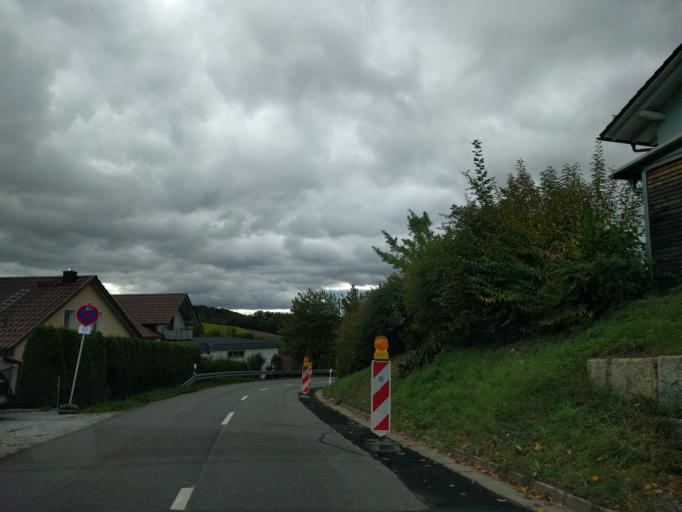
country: DE
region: Bavaria
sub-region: Lower Bavaria
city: Deggendorf
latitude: 48.8341
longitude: 12.9756
